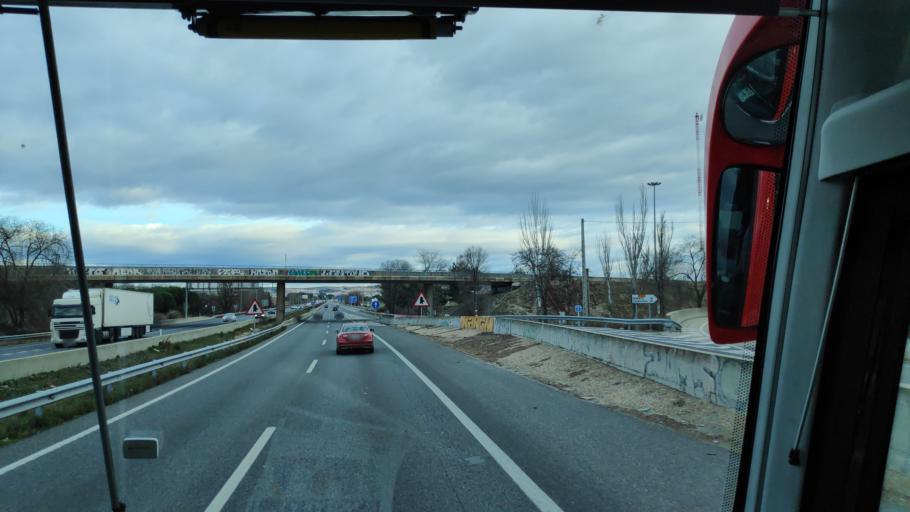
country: ES
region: Madrid
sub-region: Provincia de Madrid
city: Vaciamadrid
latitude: 40.3172
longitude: -3.5106
